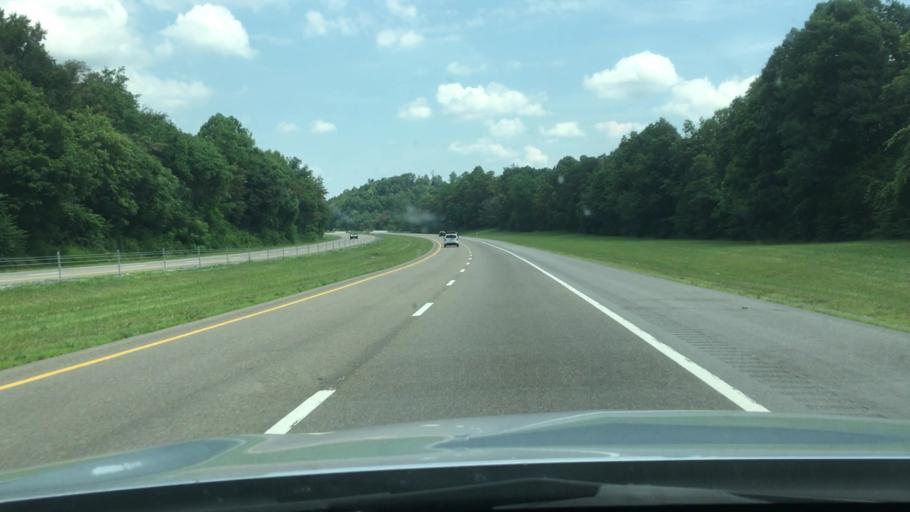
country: US
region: Tennessee
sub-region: Unicoi County
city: Unicoi
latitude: 36.2369
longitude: -82.3292
